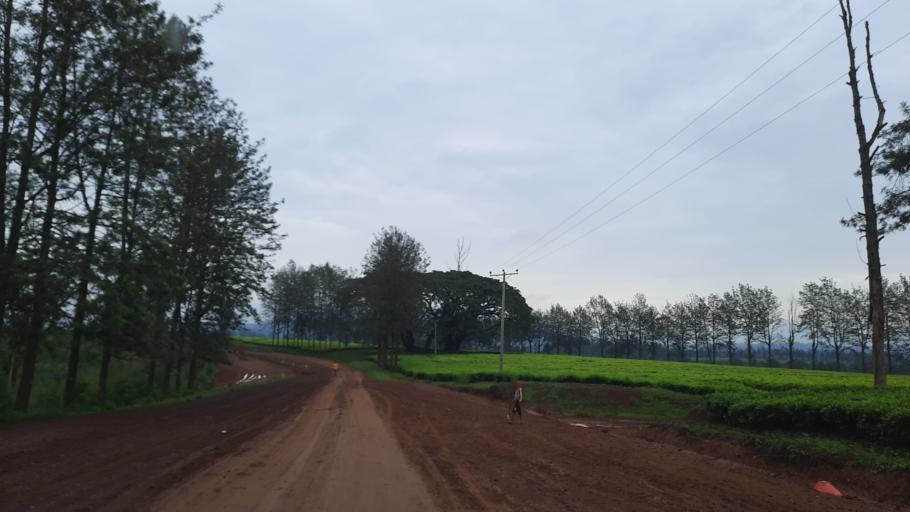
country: ET
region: Oromiya
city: Gore
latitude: 7.8429
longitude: 35.4763
